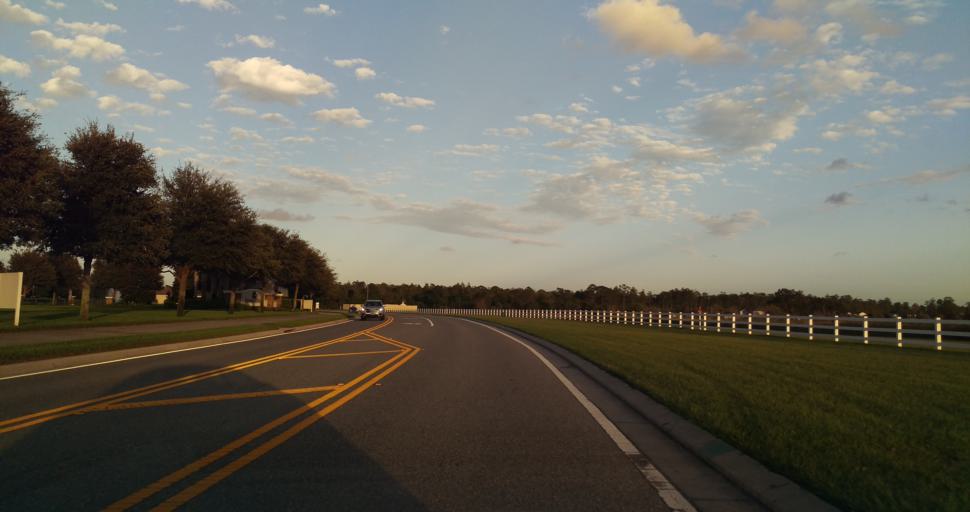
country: US
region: Florida
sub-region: Orange County
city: Lake Butler
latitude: 28.4459
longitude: -81.6047
